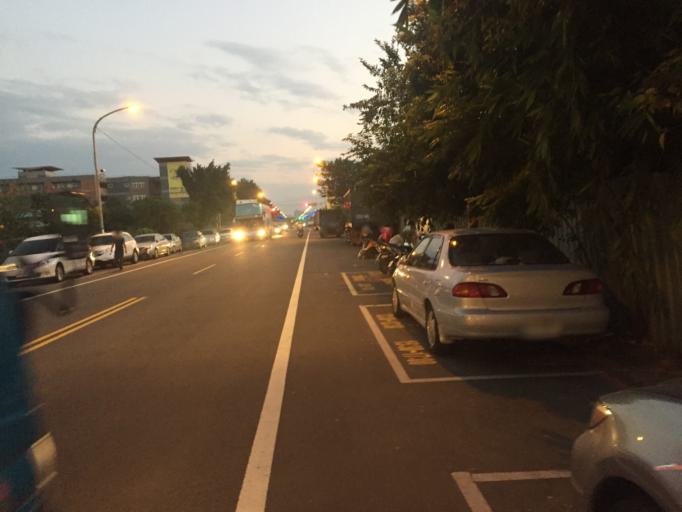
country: TW
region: Taiwan
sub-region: Taoyuan
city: Taoyuan
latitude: 24.9788
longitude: 121.3145
